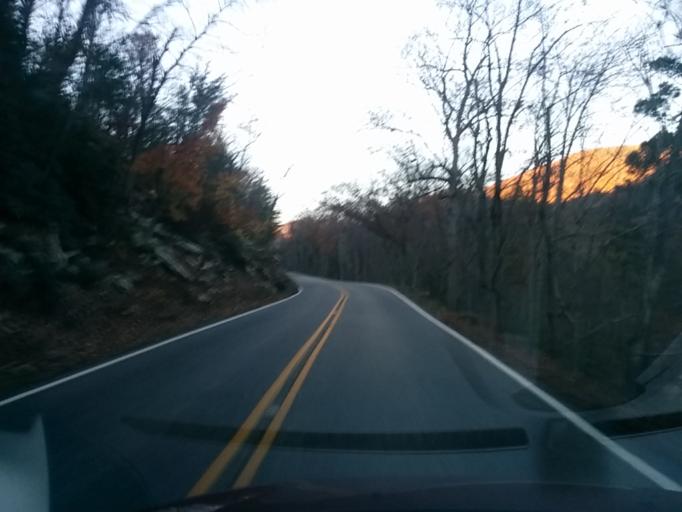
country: US
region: Virginia
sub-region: Rockbridge County
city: East Lexington
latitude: 37.9327
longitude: -79.4461
